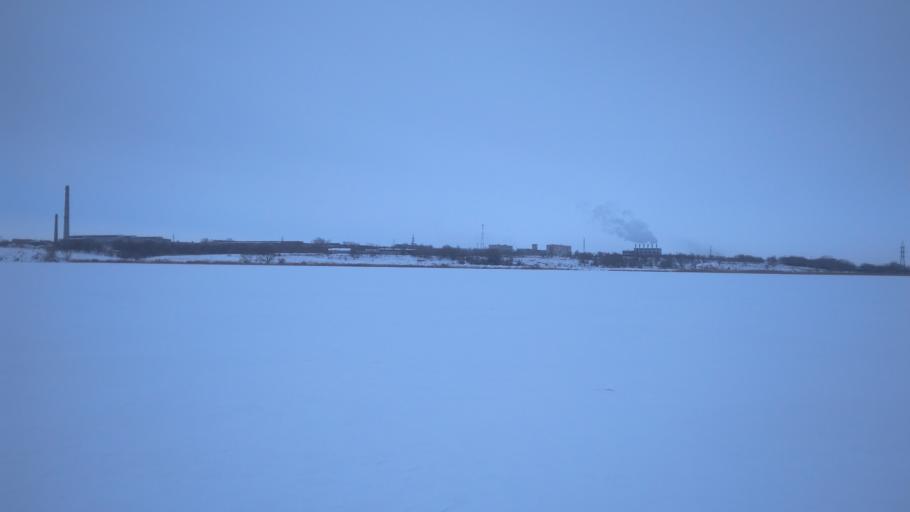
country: RU
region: Chelyabinsk
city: Troitsk
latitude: 54.0803
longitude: 61.5736
